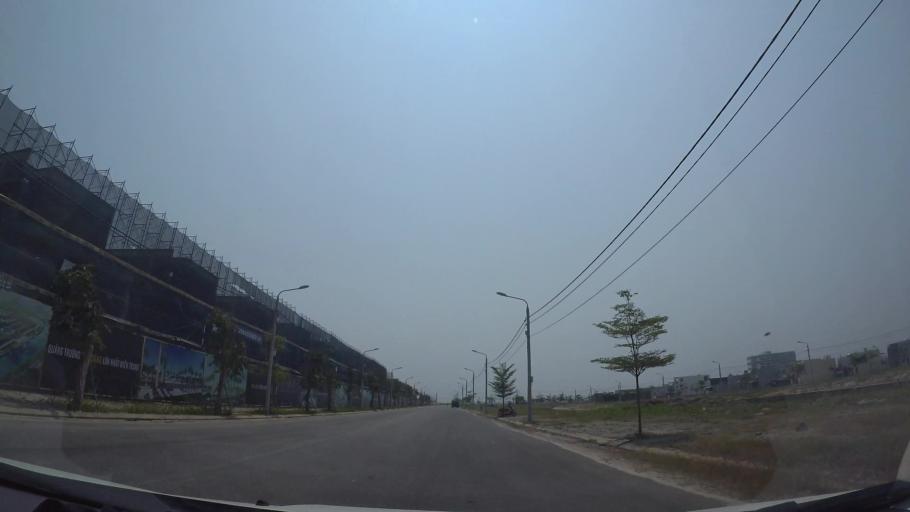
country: VN
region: Da Nang
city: Ngu Hanh Son
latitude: 15.9885
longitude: 108.2629
